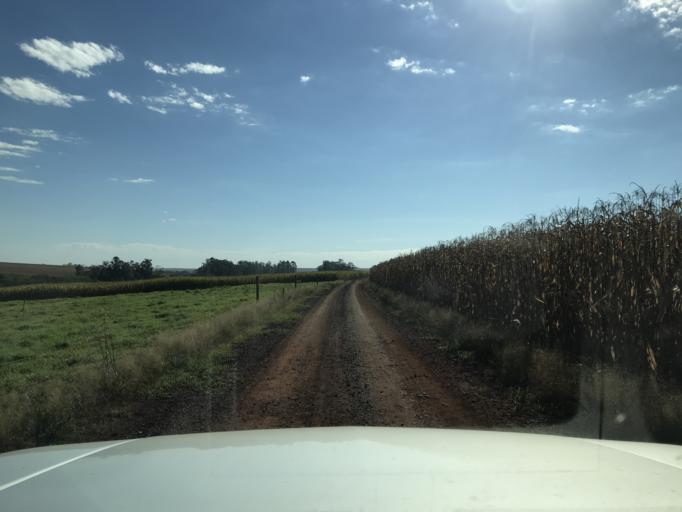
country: BR
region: Parana
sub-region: Palotina
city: Palotina
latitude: -24.2649
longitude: -53.8141
